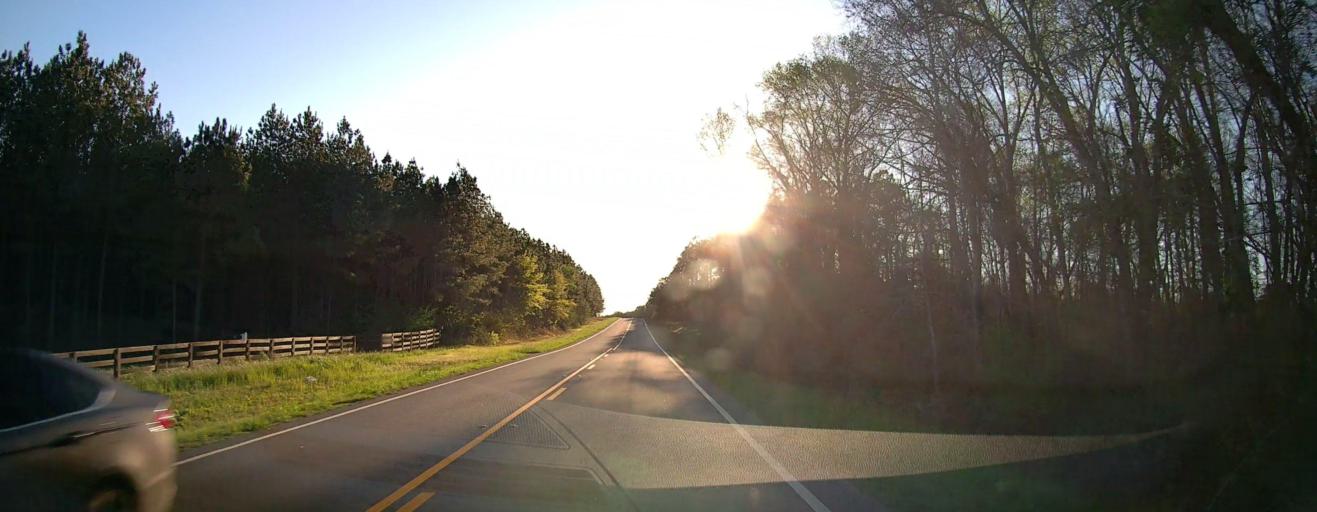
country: US
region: Georgia
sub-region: Wilcox County
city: Abbeville
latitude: 31.9867
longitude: -83.3374
